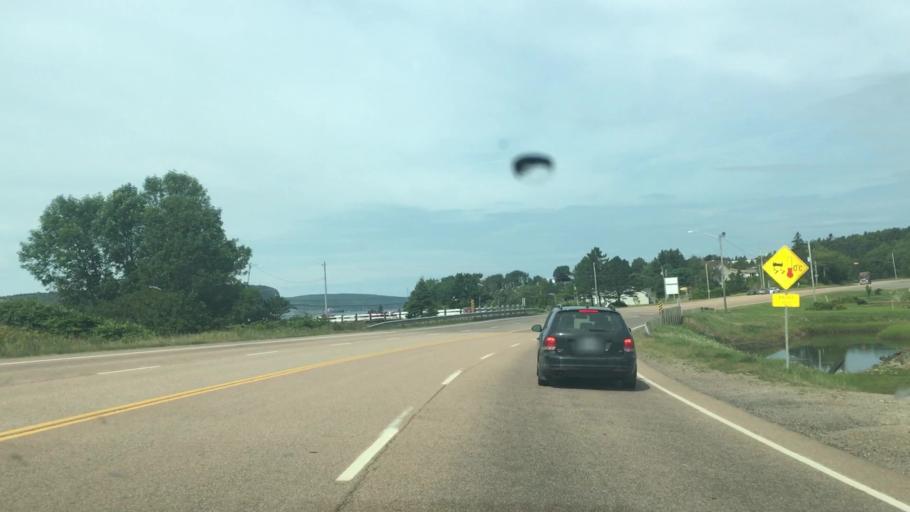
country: CA
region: Nova Scotia
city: Port Hawkesbury
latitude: 45.6217
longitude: -61.3635
